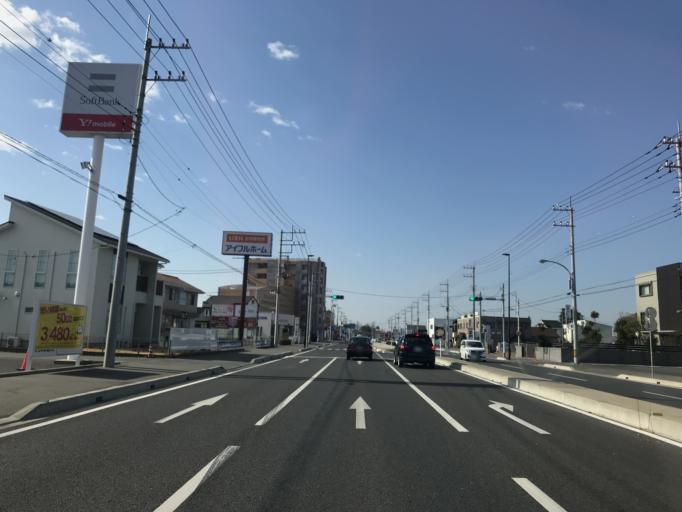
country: JP
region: Ibaraki
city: Mito-shi
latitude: 36.3401
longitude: 140.4626
